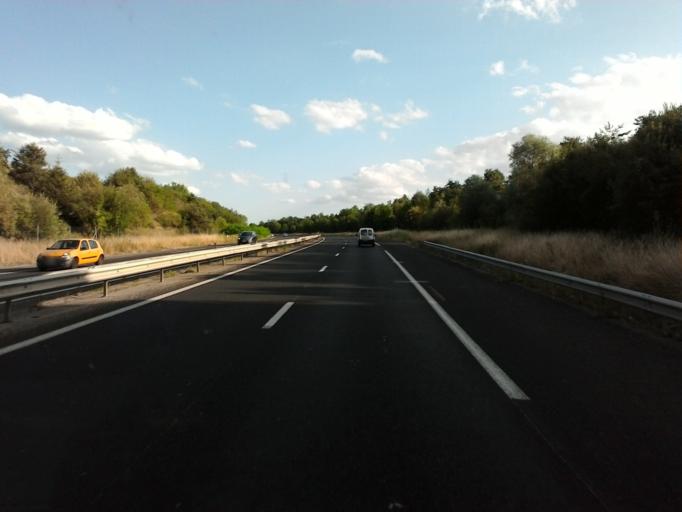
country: FR
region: Lorraine
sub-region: Departement de Meurthe-et-Moselle
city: Flavigny-sur-Moselle
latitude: 48.5672
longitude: 6.1759
